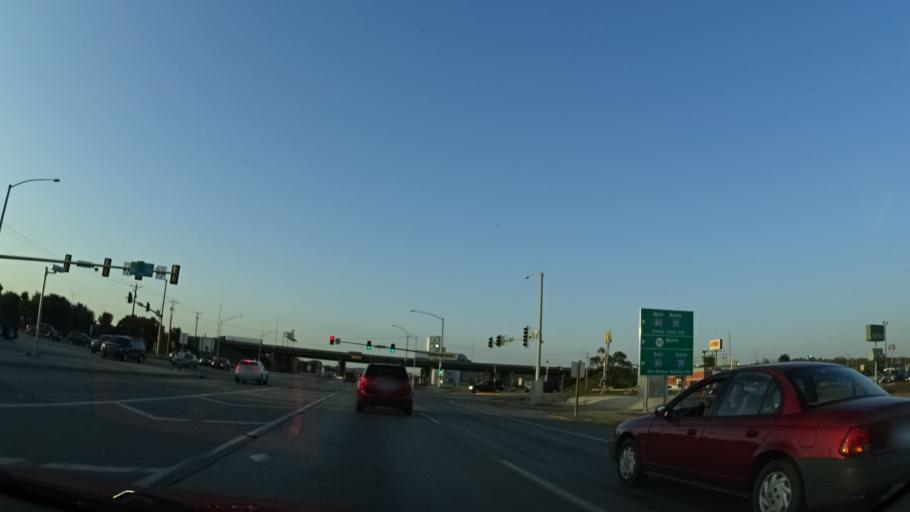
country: US
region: Iowa
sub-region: Pottawattamie County
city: Council Bluffs
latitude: 41.2300
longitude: -95.8513
